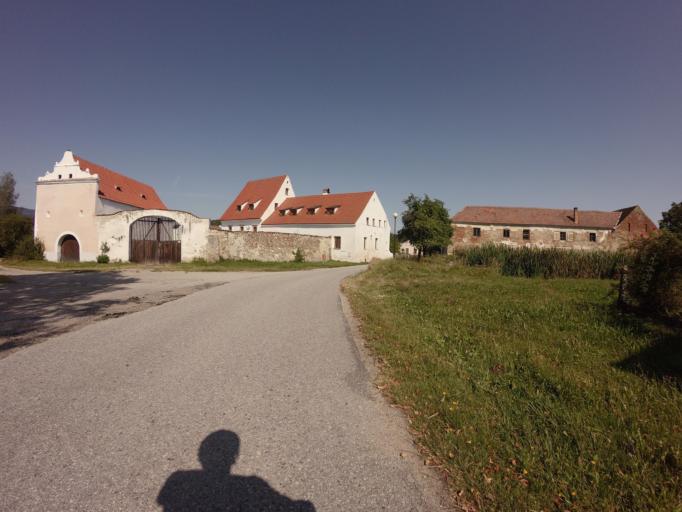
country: CZ
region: Jihocesky
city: Kamenny Ujezd
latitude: 48.8653
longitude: 14.3789
